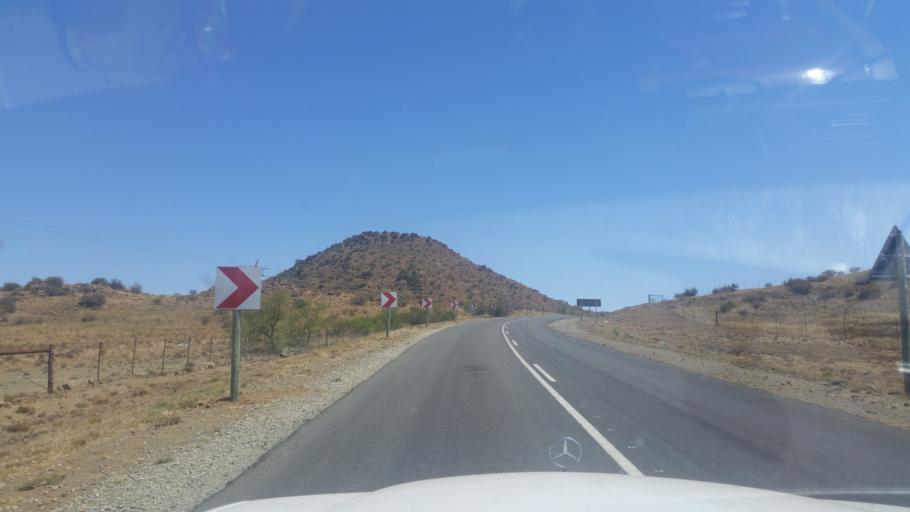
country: ZA
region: Northern Cape
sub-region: Pixley ka Seme District Municipality
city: Colesberg
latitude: -30.6379
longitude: 25.4583
